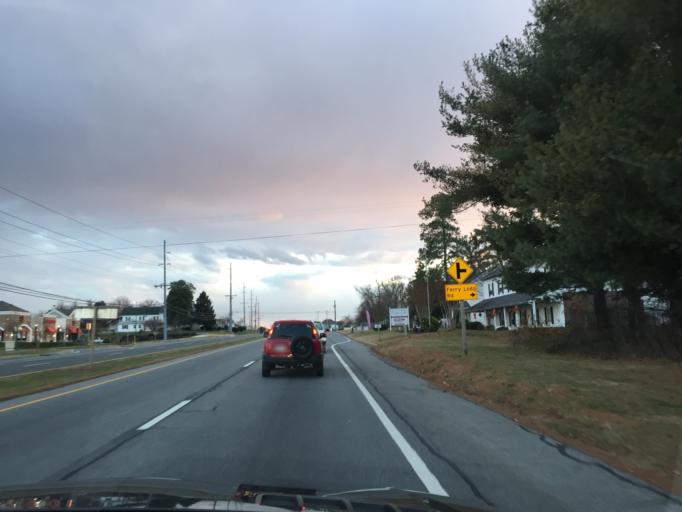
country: US
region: Maryland
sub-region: Calvert County
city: Dunkirk
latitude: 38.7244
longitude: -76.6604
